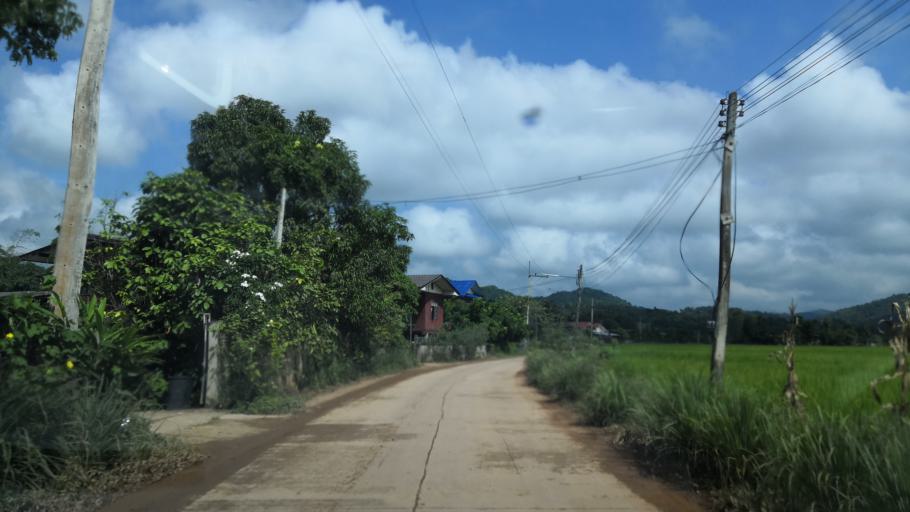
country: TH
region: Chiang Rai
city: Wiang Chiang Rung
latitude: 20.0123
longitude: 100.0406
